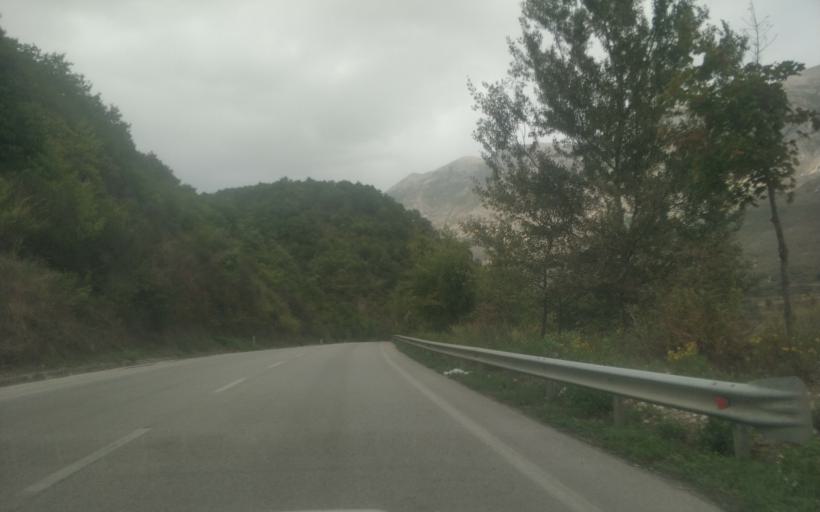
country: AL
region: Gjirokaster
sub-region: Rrethi i Gjirokastres
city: Picar
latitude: 40.2181
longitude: 20.0858
